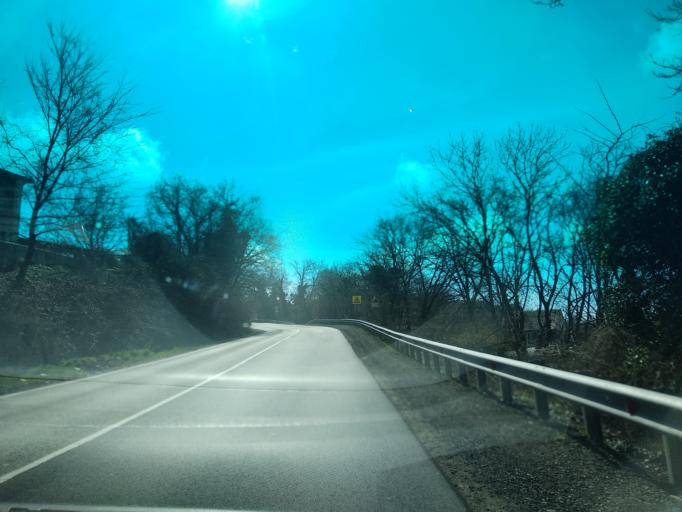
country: RU
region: Krasnodarskiy
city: Tuapse
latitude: 44.0892
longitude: 39.1230
